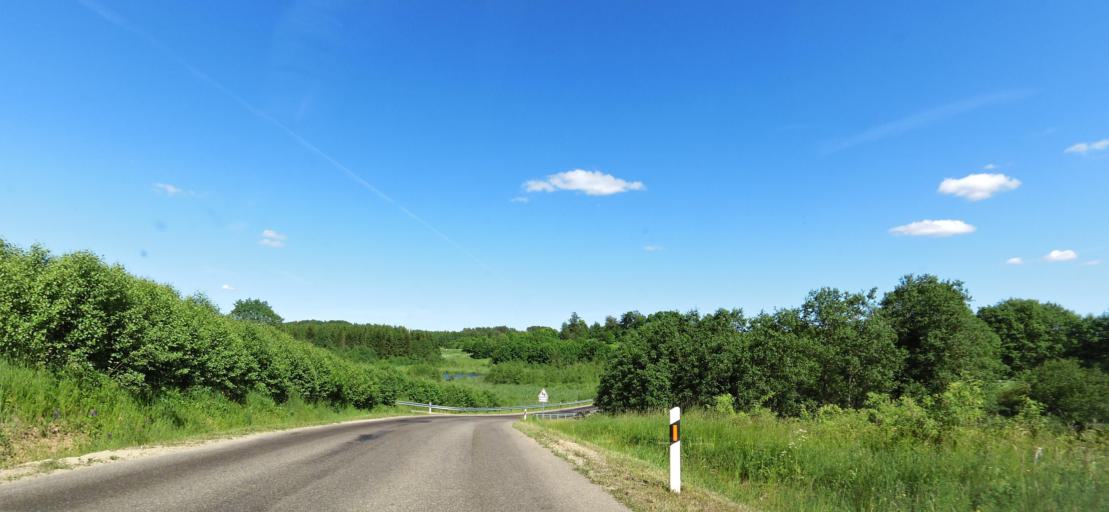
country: LT
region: Utenos apskritis
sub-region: Anyksciai
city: Anyksciai
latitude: 55.3204
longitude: 25.1237
